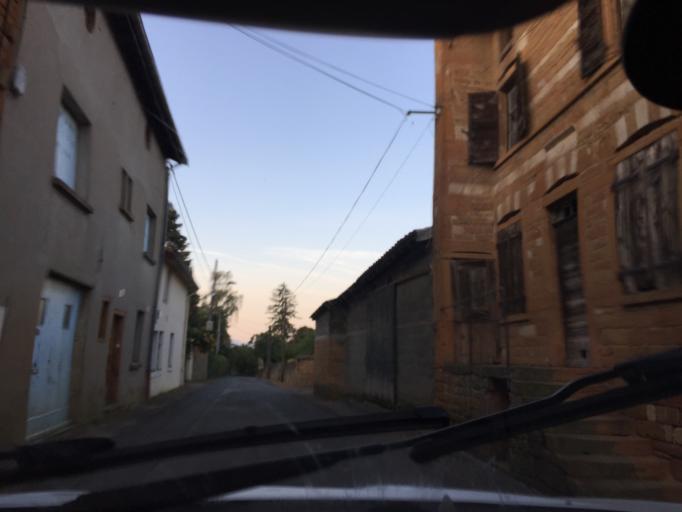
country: FR
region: Rhone-Alpes
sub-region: Departement du Rhone
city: Charnay
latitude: 45.9138
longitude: 4.6560
